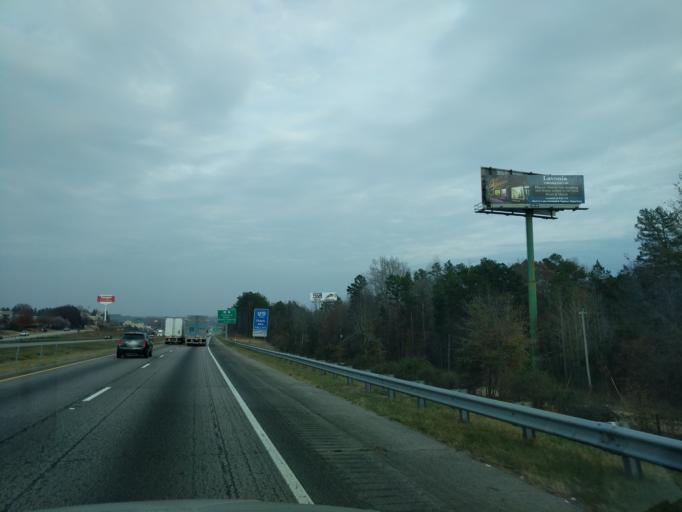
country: US
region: Georgia
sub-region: Jackson County
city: Commerce
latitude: 34.2466
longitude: -83.4773
